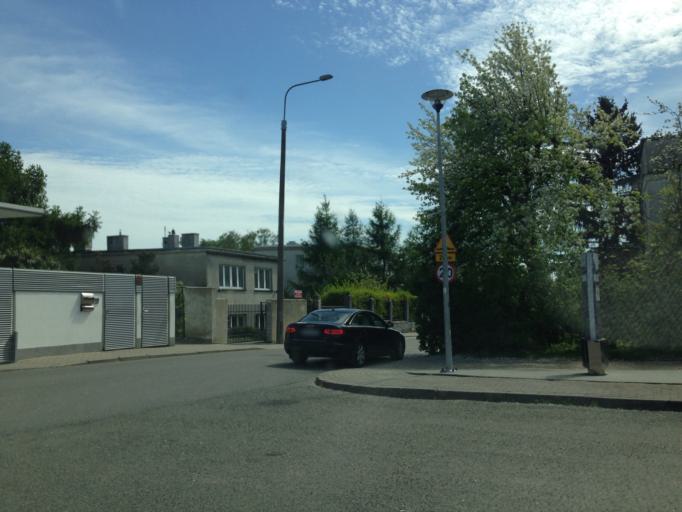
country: PL
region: Pomeranian Voivodeship
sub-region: Gdynia
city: Gdynia
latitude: 54.5143
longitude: 18.5448
